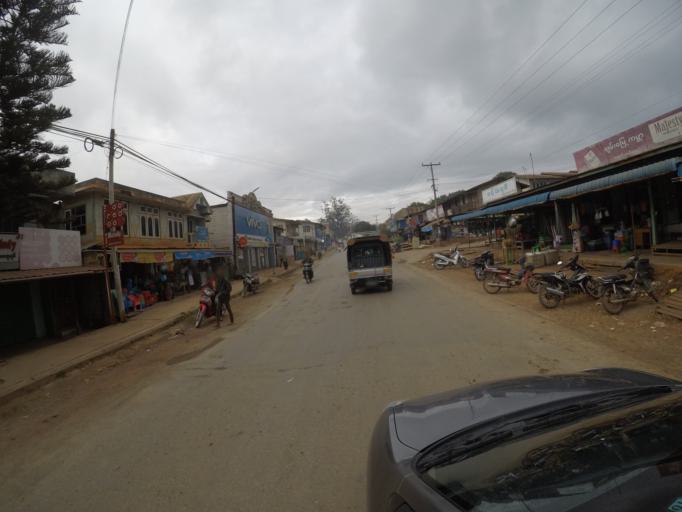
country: MM
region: Shan
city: Taunggyi
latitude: 20.7772
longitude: 96.9985
